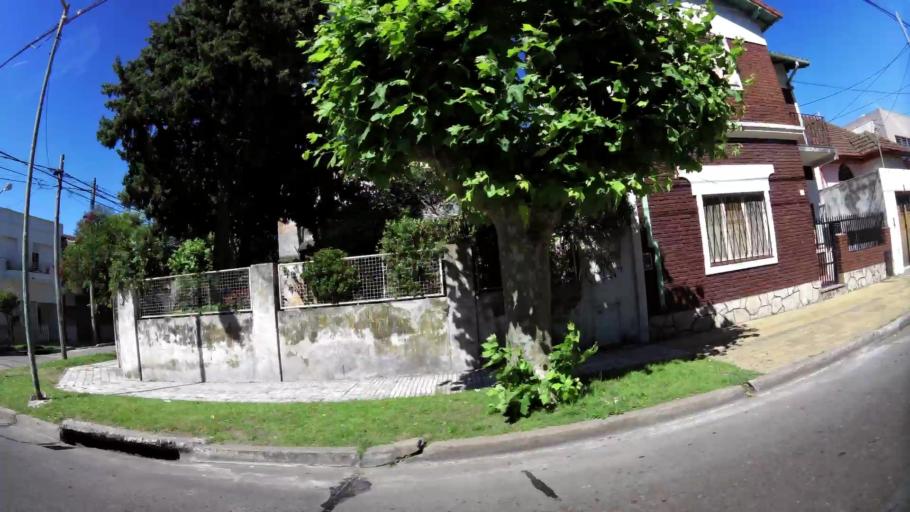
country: AR
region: Buenos Aires
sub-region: Partido de General San Martin
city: General San Martin
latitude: -34.5676
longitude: -58.5359
